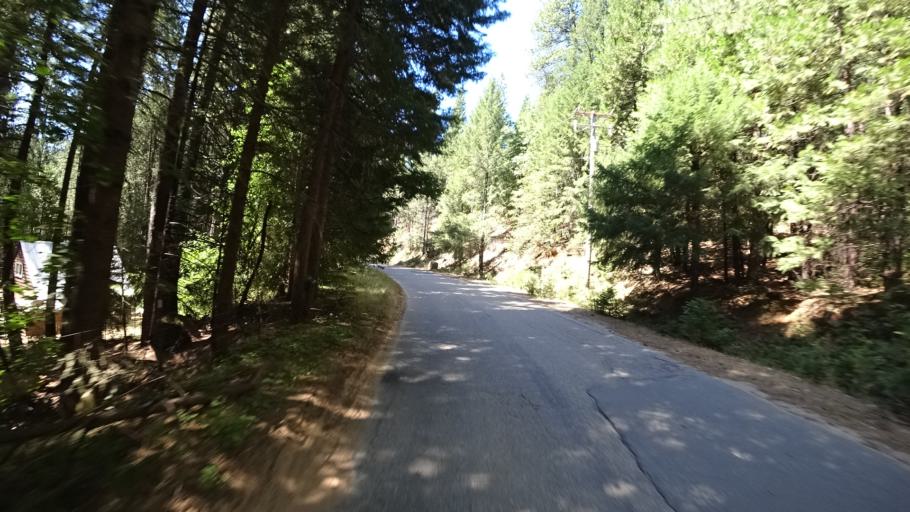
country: US
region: California
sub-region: Amador County
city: Pioneer
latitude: 38.4232
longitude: -120.4923
